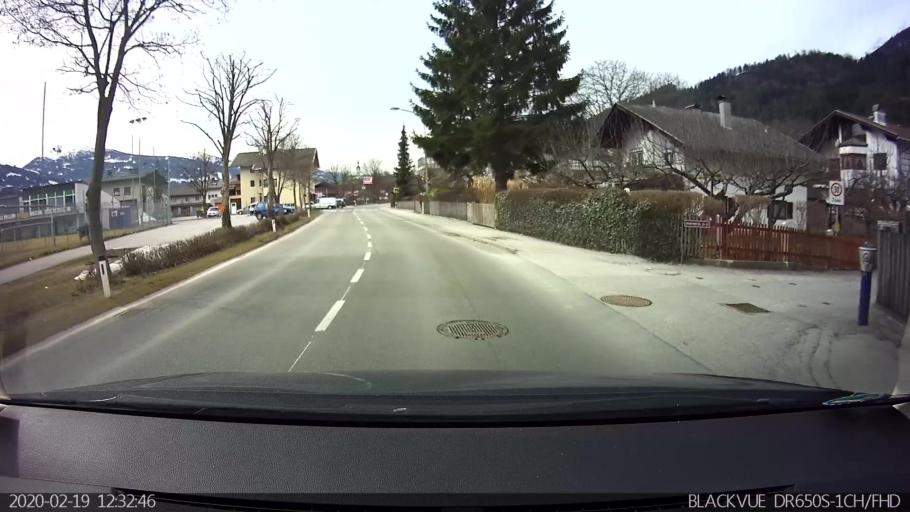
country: AT
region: Tyrol
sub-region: Politischer Bezirk Schwaz
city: Vomp
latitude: 47.3457
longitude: 11.6917
